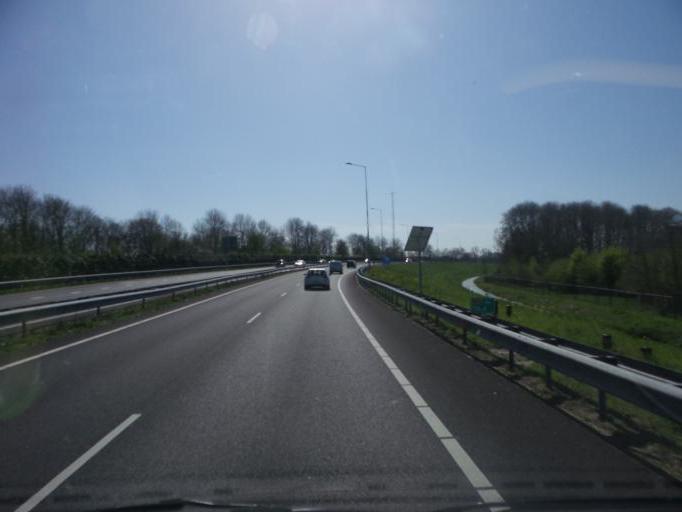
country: NL
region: South Holland
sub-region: Bodegraven-Reeuwijk
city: Bodegraven
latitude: 52.0841
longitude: 4.7376
